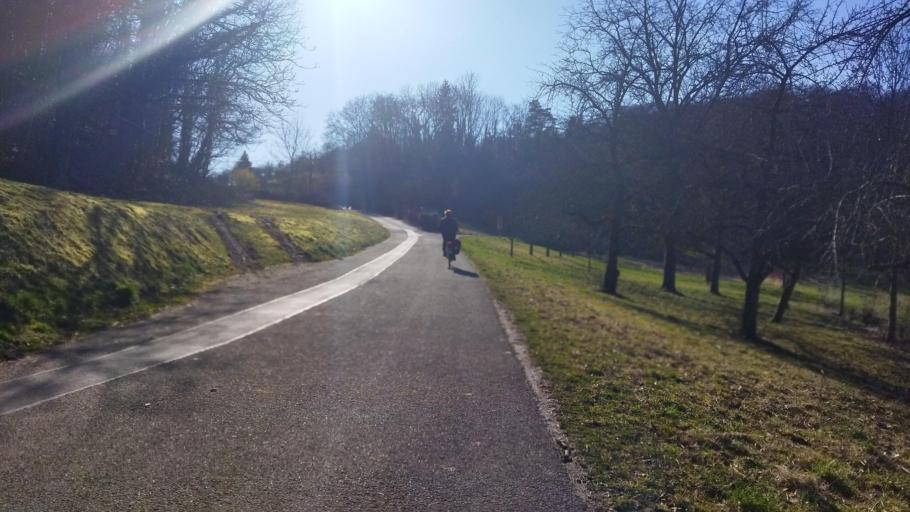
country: DE
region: Baden-Wuerttemberg
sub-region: Regierungsbezirk Stuttgart
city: Besigheim
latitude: 49.0085
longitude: 9.1413
